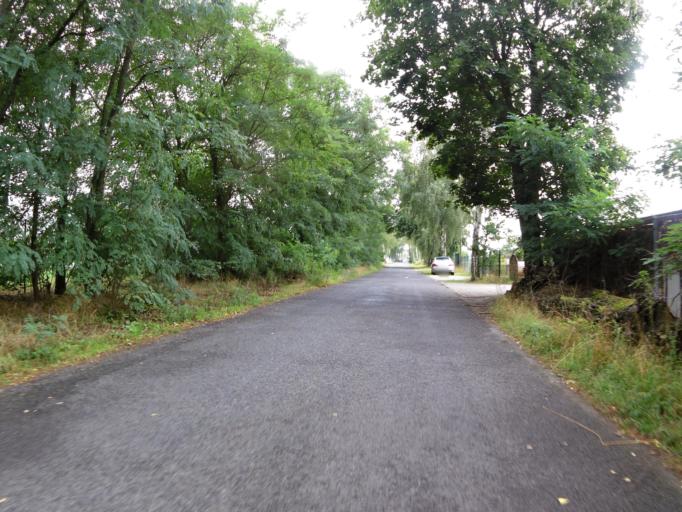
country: DE
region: Brandenburg
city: Storkow
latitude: 52.2707
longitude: 13.9432
